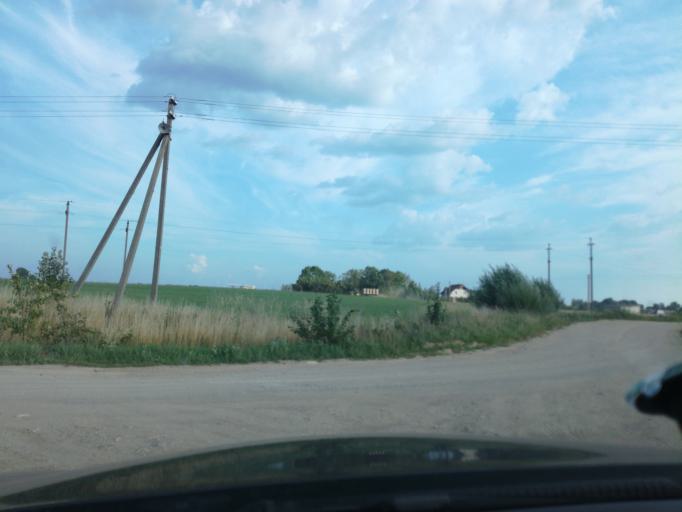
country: LT
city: Simnas
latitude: 54.3927
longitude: 23.8167
